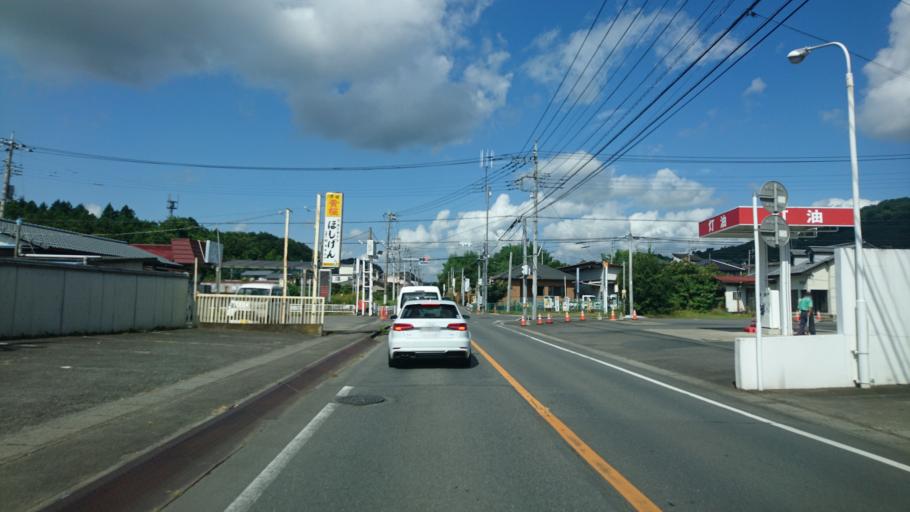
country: JP
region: Gunma
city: Omamacho-omama
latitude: 36.4314
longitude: 139.3051
